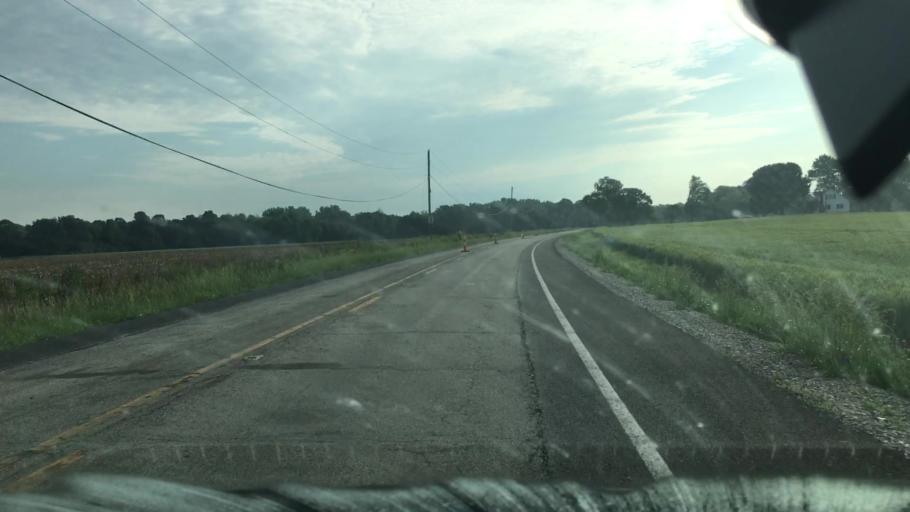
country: US
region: Kentucky
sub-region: Hancock County
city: Lewisport
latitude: 37.9465
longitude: -86.9716
